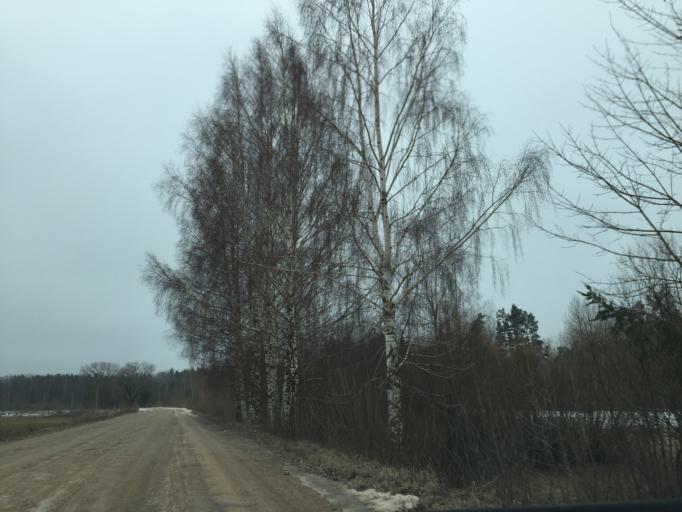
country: LV
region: Ozolnieku
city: Ozolnieki
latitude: 56.6345
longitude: 23.8016
